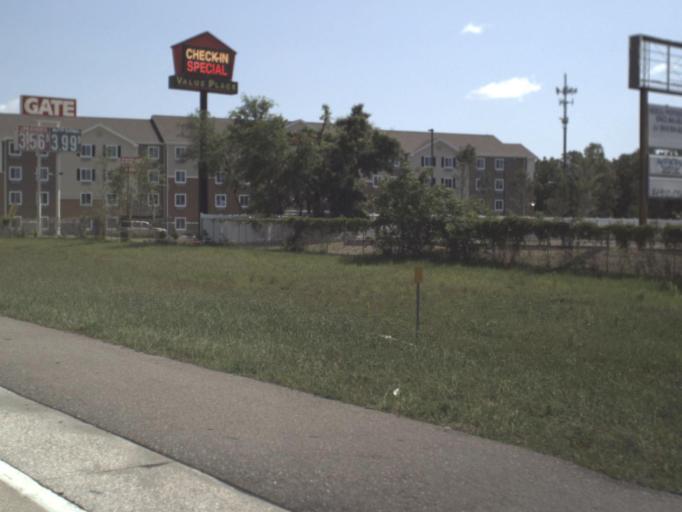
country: US
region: Florida
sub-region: Duval County
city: Jacksonville
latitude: 30.4265
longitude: -81.6562
